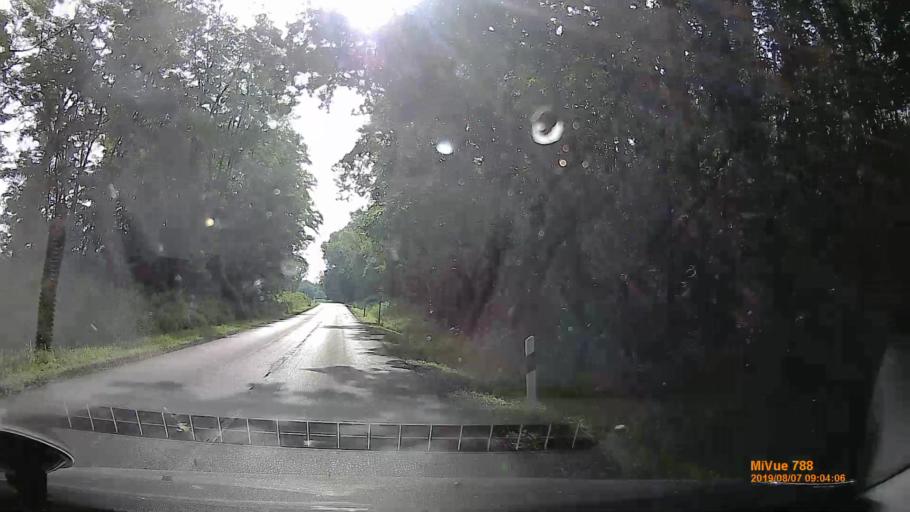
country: HU
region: Zala
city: Pacsa
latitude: 46.7279
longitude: 16.9930
